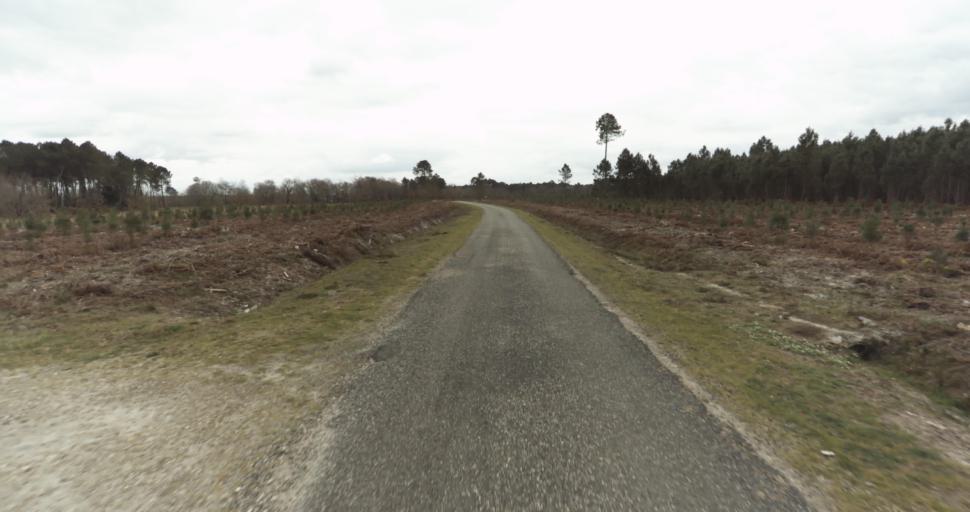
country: FR
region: Aquitaine
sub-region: Departement des Landes
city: Sarbazan
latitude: 44.0153
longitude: -0.2981
